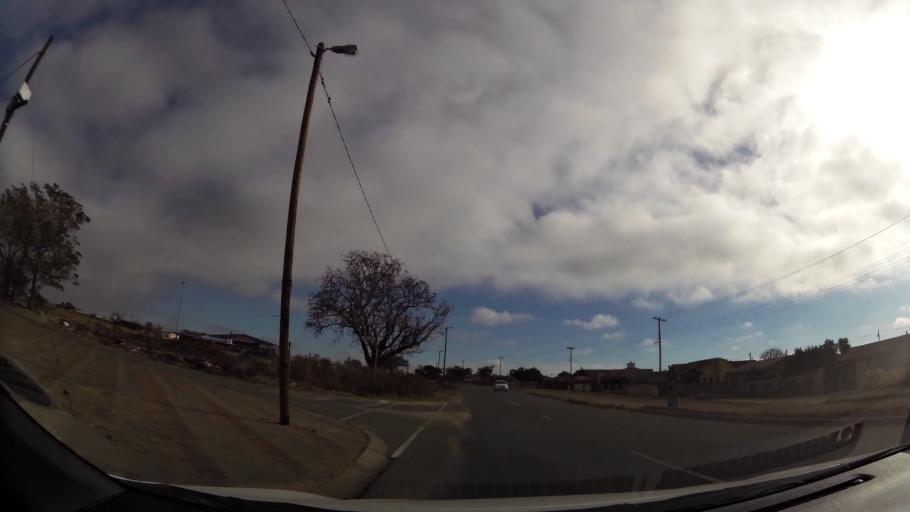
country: ZA
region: Limpopo
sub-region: Capricorn District Municipality
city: Polokwane
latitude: -23.8526
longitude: 29.3845
